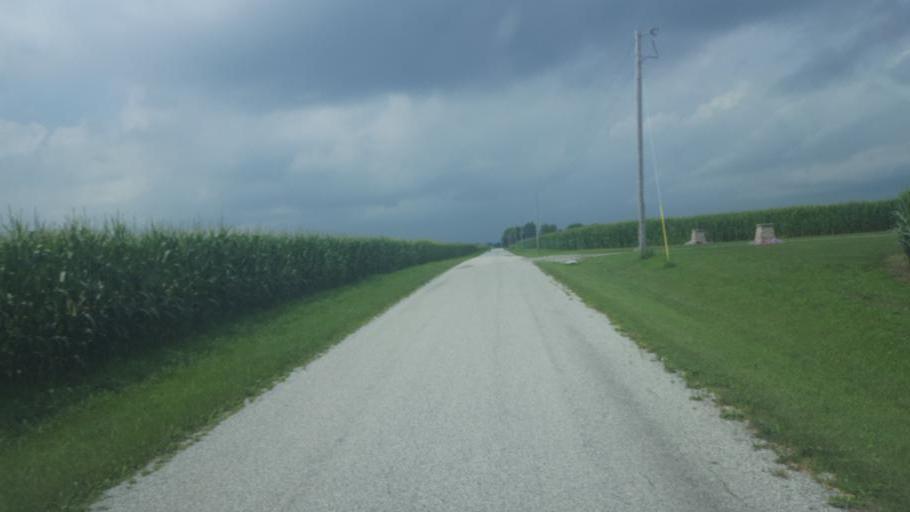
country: US
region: Ohio
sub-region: Union County
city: Richwood
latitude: 40.5217
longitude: -83.3247
